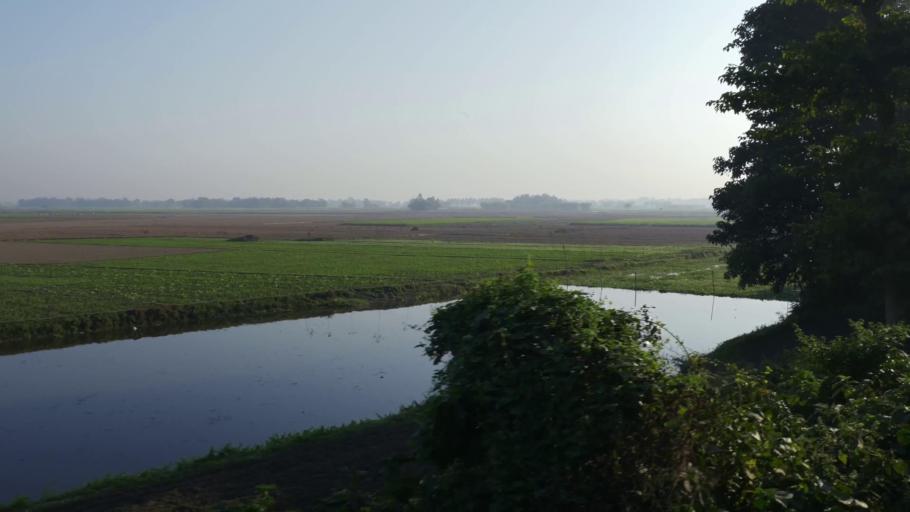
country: BD
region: Dhaka
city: Jamalpur
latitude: 24.9253
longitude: 89.9367
